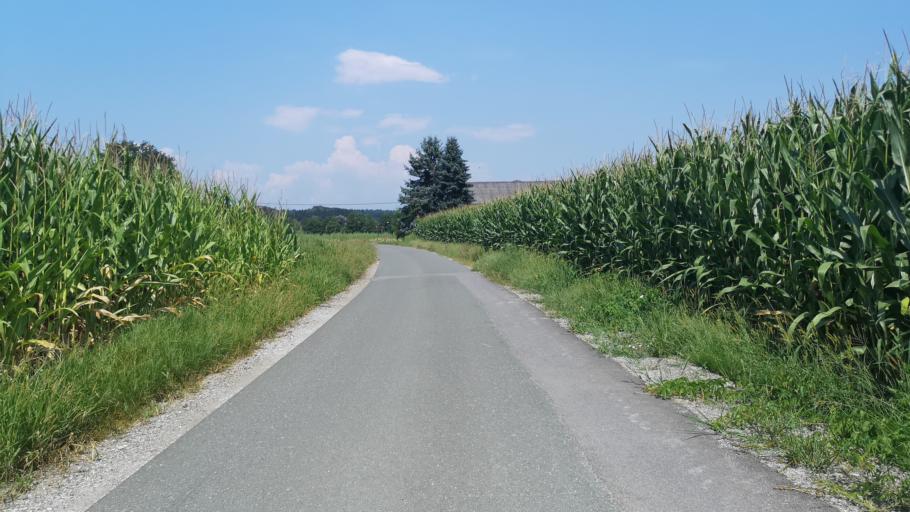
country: AT
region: Styria
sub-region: Politischer Bezirk Deutschlandsberg
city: Gross Sankt Florian
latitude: 46.8157
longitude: 15.3029
